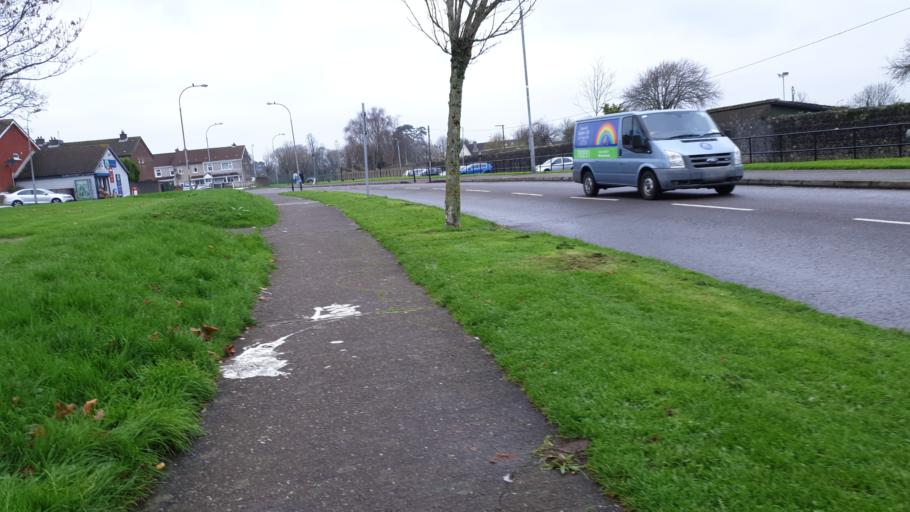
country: IE
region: Munster
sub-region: County Cork
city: Passage West
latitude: 51.8893
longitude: -8.3998
